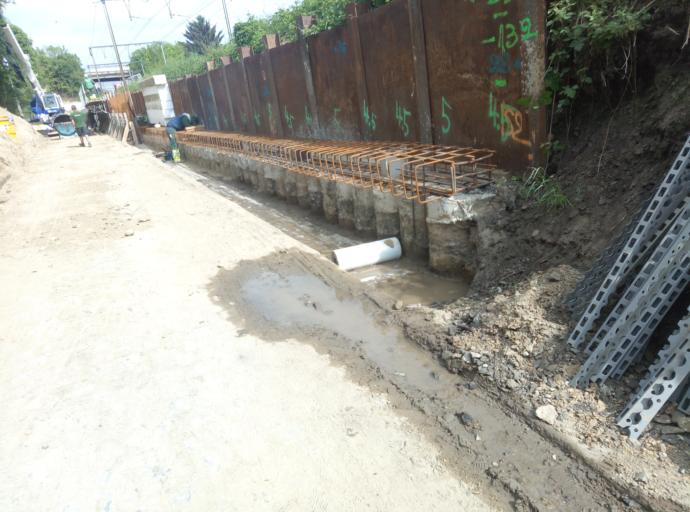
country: BE
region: Flanders
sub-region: Provincie Vlaams-Brabant
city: Leuven
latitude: 50.8589
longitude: 4.7324
